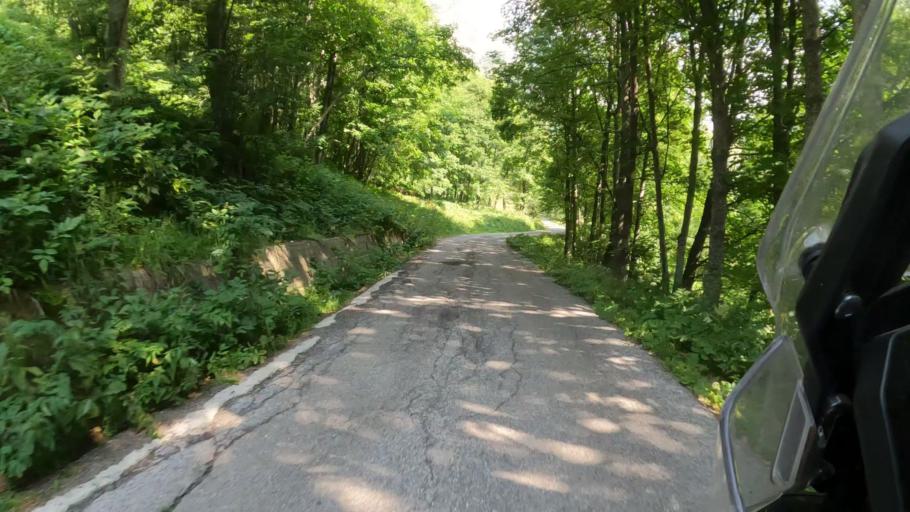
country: IT
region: Piedmont
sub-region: Provincia di Cuneo
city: Canosio
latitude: 44.4304
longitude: 7.0538
